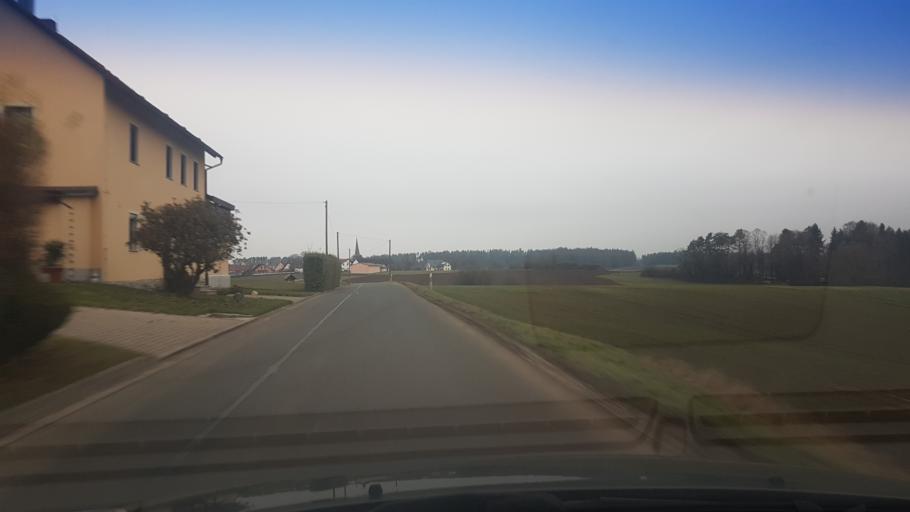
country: DE
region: Bavaria
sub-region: Upper Franconia
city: Stadelhofen
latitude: 50.0291
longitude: 11.2407
